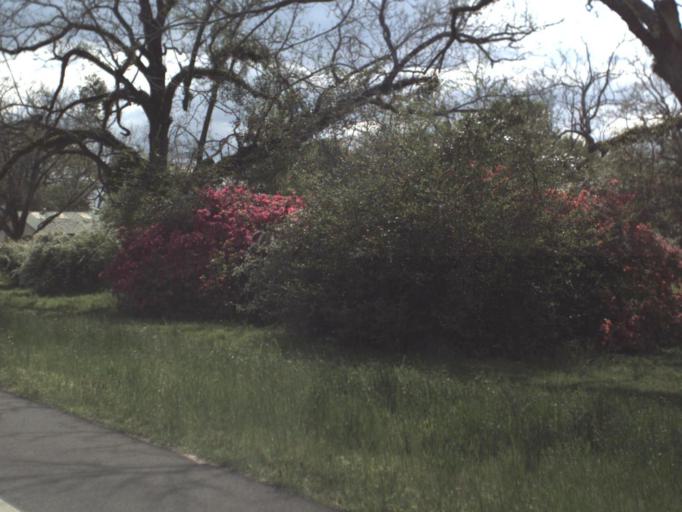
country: US
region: Florida
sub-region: Okaloosa County
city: Crestview
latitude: 30.9114
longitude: -86.4877
